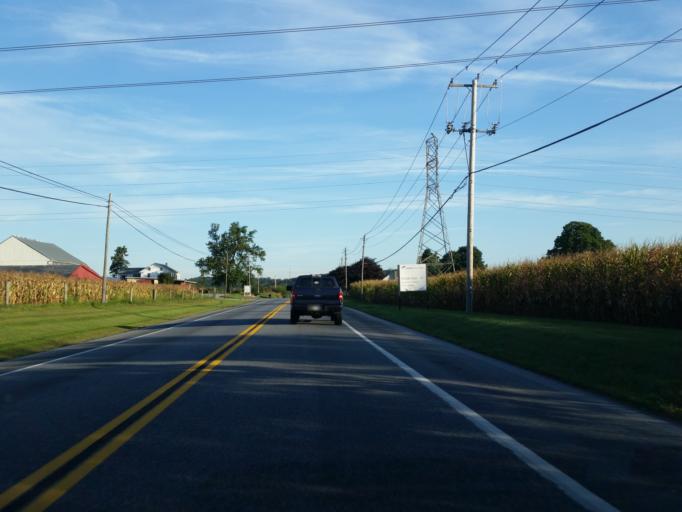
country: US
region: Pennsylvania
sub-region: Lancaster County
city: Quarryville
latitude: 39.8633
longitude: -76.2254
